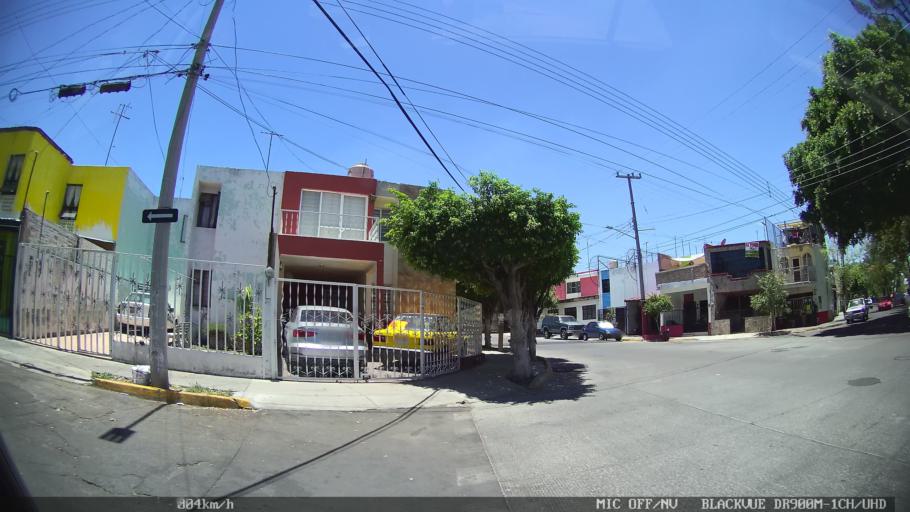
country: MX
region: Jalisco
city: Tlaquepaque
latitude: 20.6750
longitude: -103.2930
